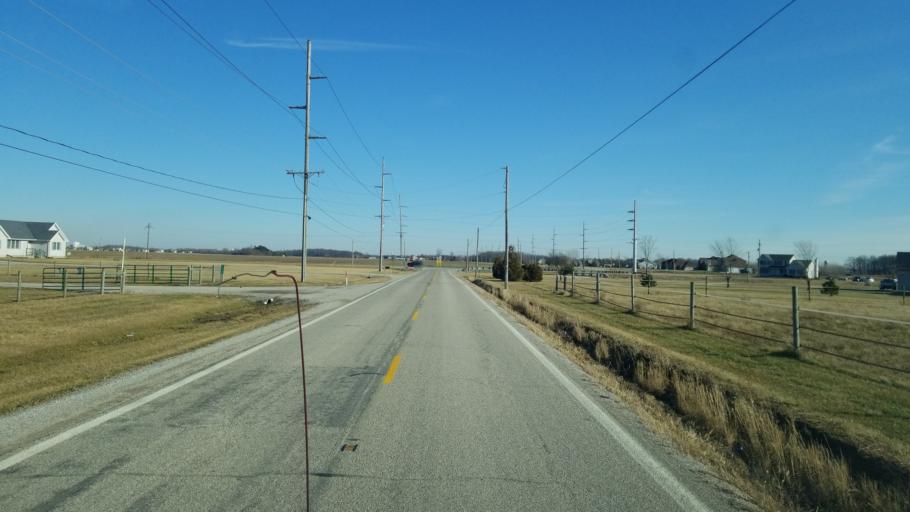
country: US
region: Ohio
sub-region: Sandusky County
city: Woodville
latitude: 41.4499
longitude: -83.4174
